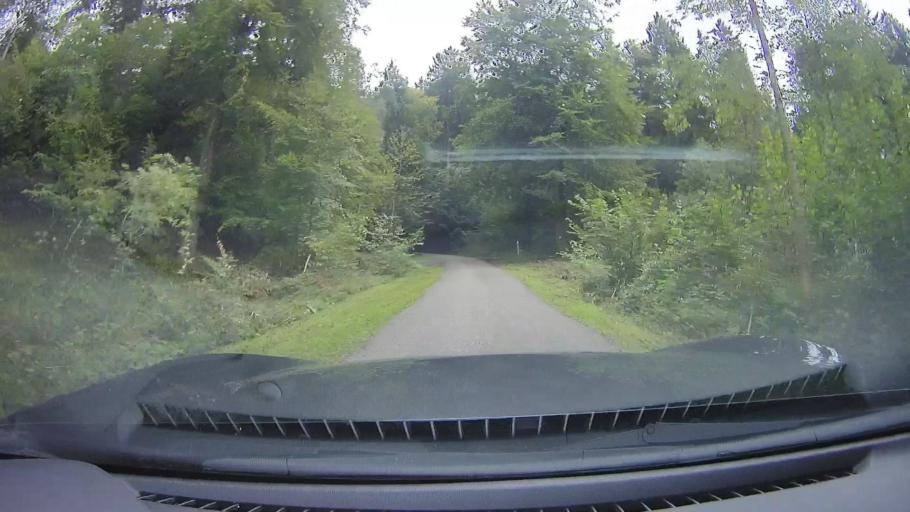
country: DE
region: Baden-Wuerttemberg
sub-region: Regierungsbezirk Stuttgart
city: Murrhardt
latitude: 48.9743
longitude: 9.5593
